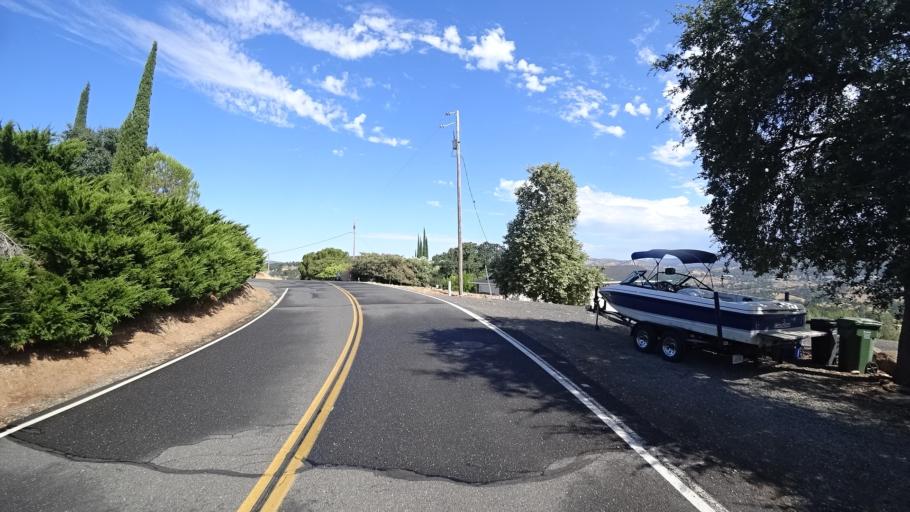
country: US
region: California
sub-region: Calaveras County
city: Copperopolis
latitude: 37.9153
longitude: -120.6141
